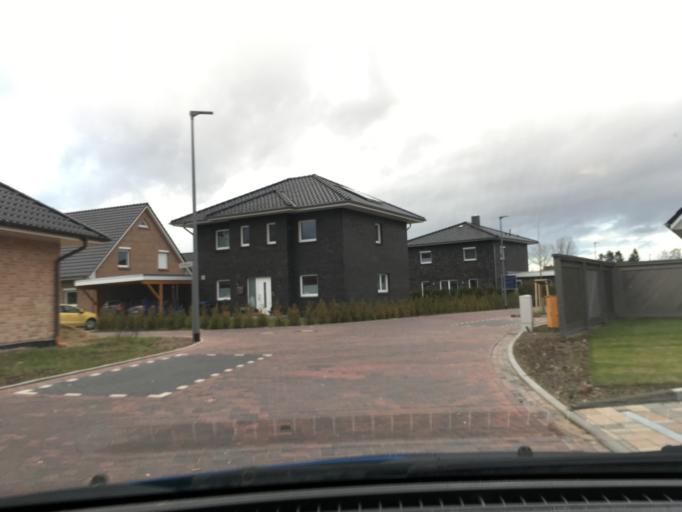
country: DE
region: Schleswig-Holstein
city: Kremperheide
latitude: 53.8982
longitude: 9.4964
